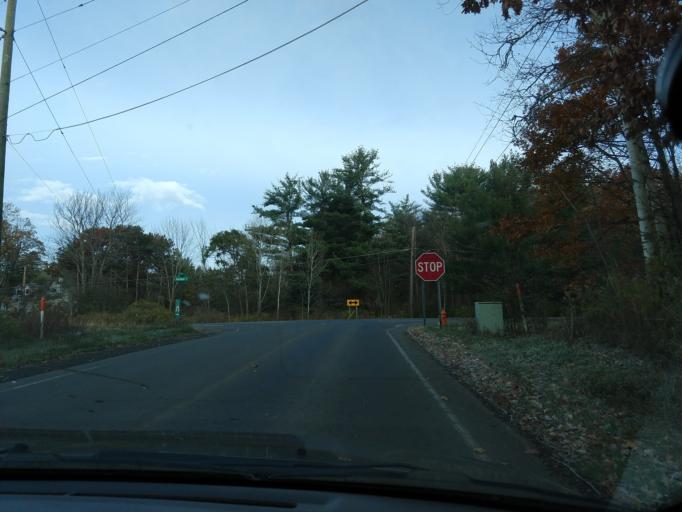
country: US
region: New York
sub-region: Tompkins County
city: Northeast Ithaca
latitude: 42.4674
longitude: -76.4481
